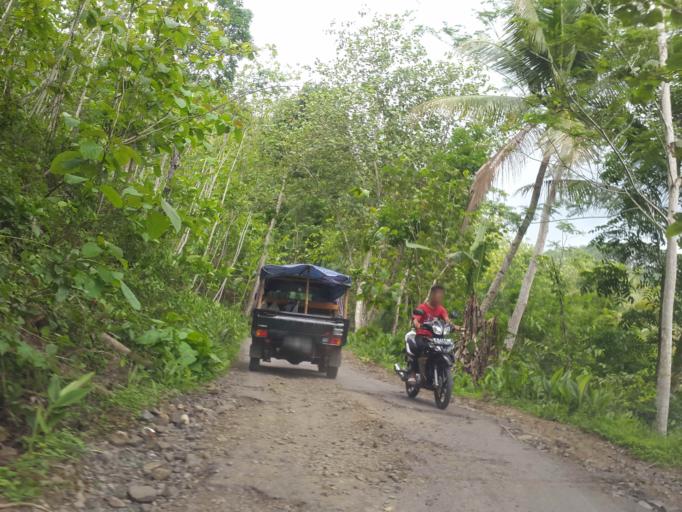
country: ID
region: Central Java
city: Genteng Wetan
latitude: -7.3588
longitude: 108.9025
